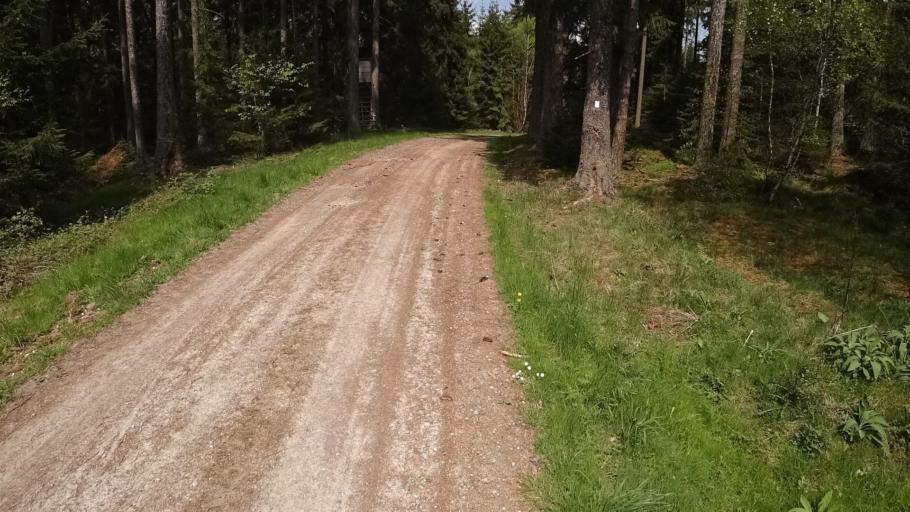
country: DE
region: Rheinland-Pfalz
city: Maisborn
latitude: 50.0674
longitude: 7.5843
